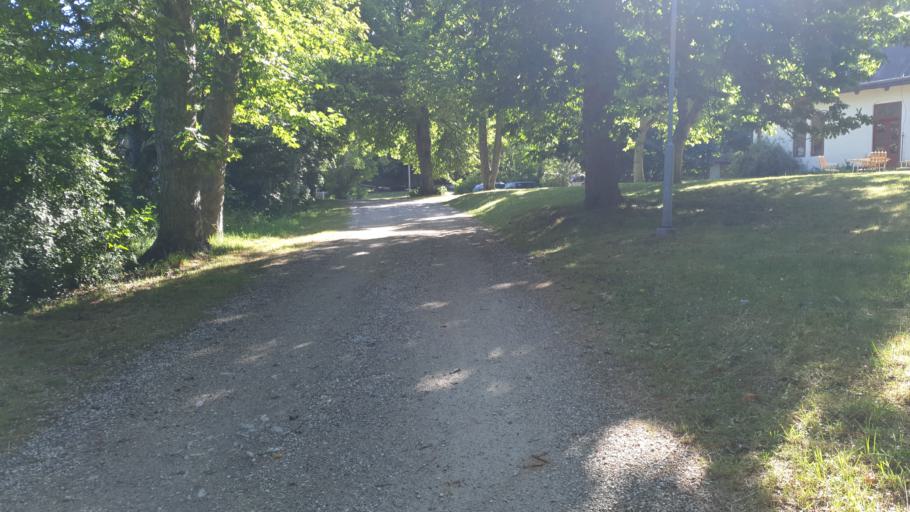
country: SE
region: Gotland
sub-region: Gotland
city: Vibble
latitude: 57.5997
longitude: 18.2154
